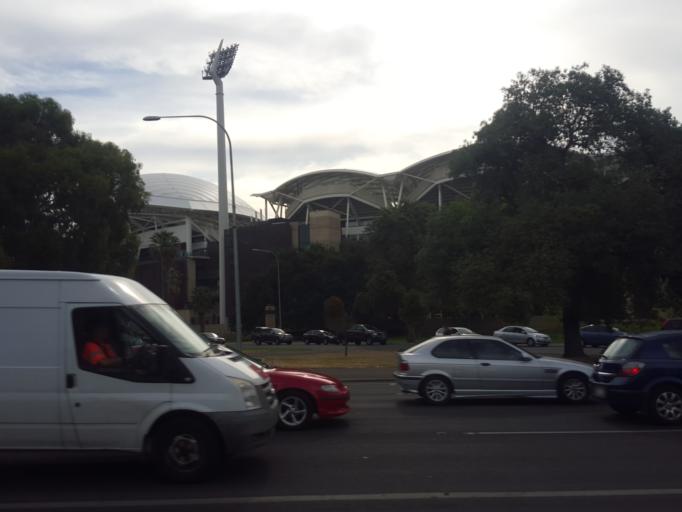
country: AU
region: South Australia
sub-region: Adelaide
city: North Adelaide
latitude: -34.9158
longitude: 138.5989
